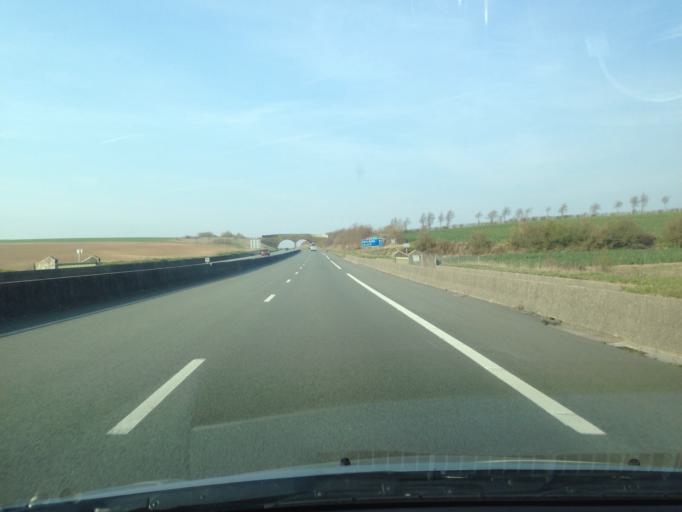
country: FR
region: Nord-Pas-de-Calais
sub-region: Departement du Pas-de-Calais
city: Verton
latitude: 50.4179
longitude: 1.6942
